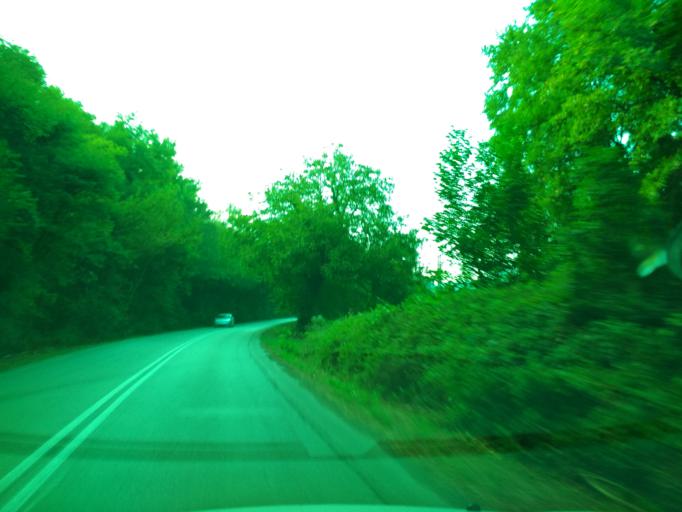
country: GR
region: Central Greece
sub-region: Nomos Evvoias
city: Prokopion
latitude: 38.7599
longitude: 23.4804
